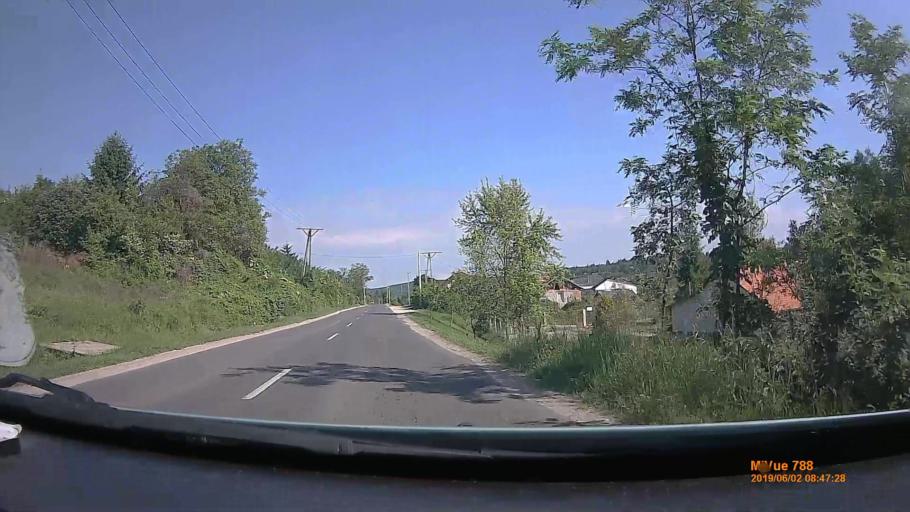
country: HU
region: Borsod-Abauj-Zemplen
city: Sajobabony
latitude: 48.1298
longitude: 20.7134
